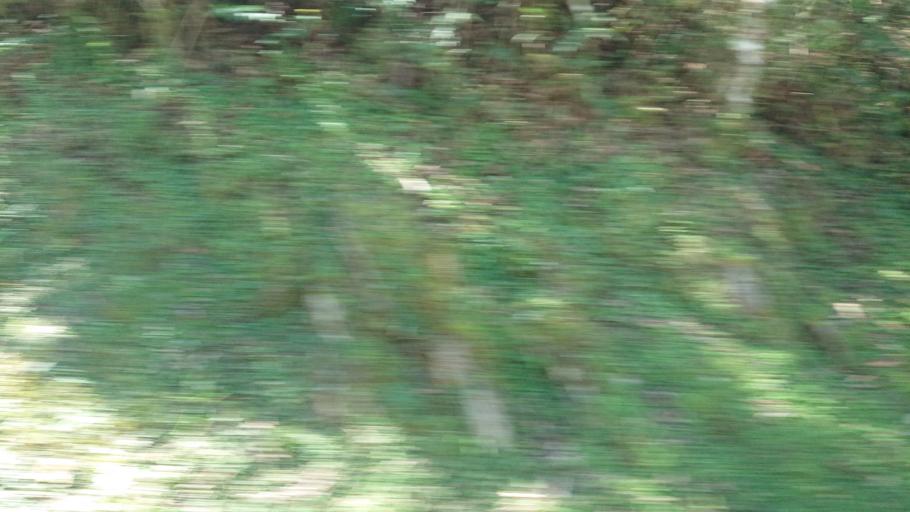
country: TW
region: Taiwan
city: Daxi
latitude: 24.4034
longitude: 121.3649
